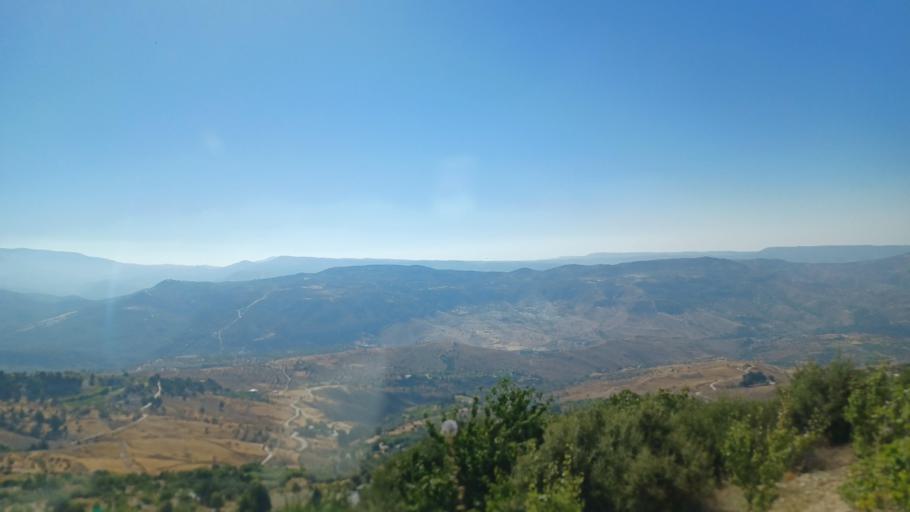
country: CY
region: Pafos
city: Mesogi
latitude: 34.8903
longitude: 32.6264
